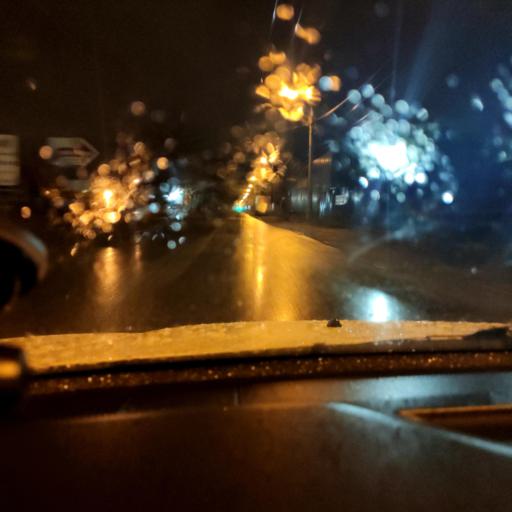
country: RU
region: Samara
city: Samara
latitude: 53.1936
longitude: 50.2741
